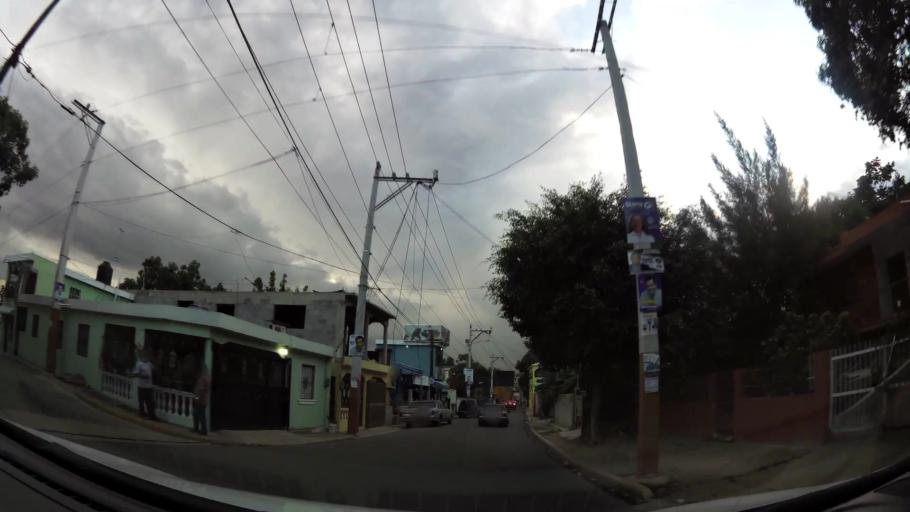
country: DO
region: Santo Domingo
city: Santo Domingo Oeste
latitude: 18.5230
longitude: -70.0186
